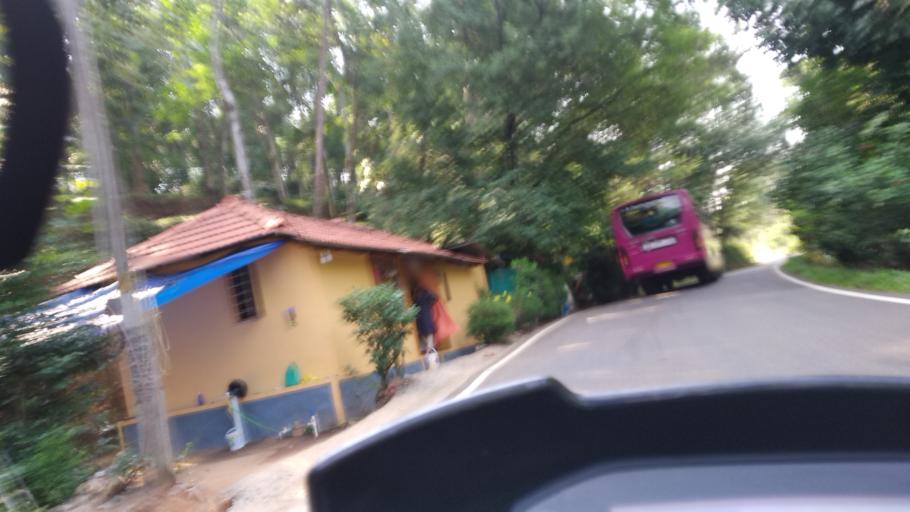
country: IN
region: Kerala
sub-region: Ernakulam
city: Piravam
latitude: 9.8172
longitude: 76.5571
